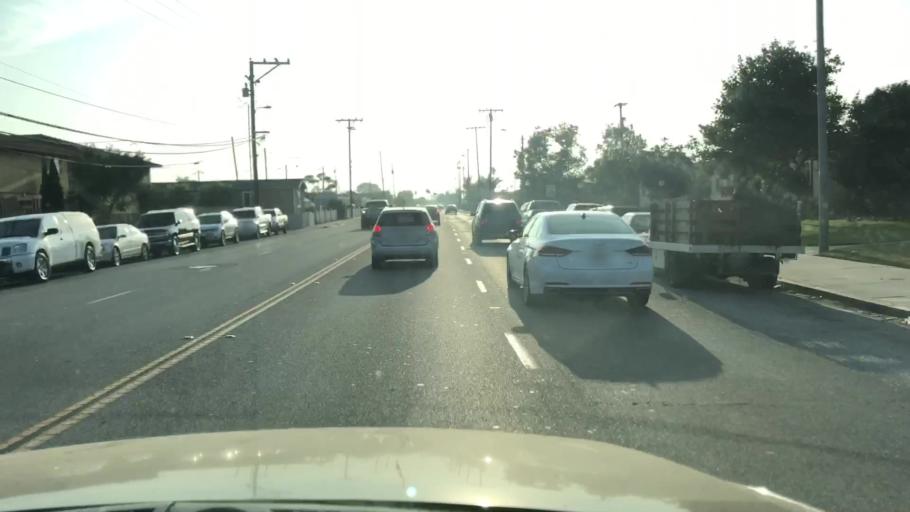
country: US
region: California
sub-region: Ventura County
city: Port Hueneme
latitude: 34.1548
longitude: -119.1741
